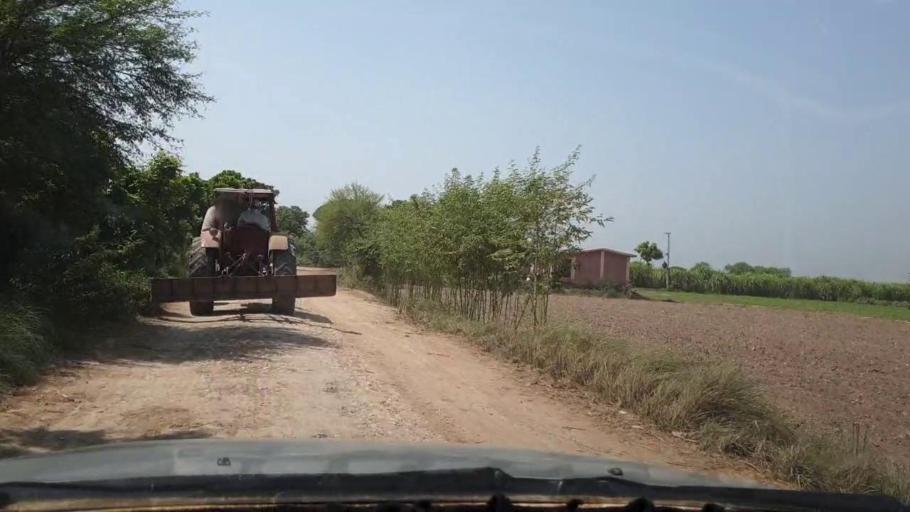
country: PK
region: Sindh
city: Tando Muhammad Khan
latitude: 25.1971
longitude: 68.6608
